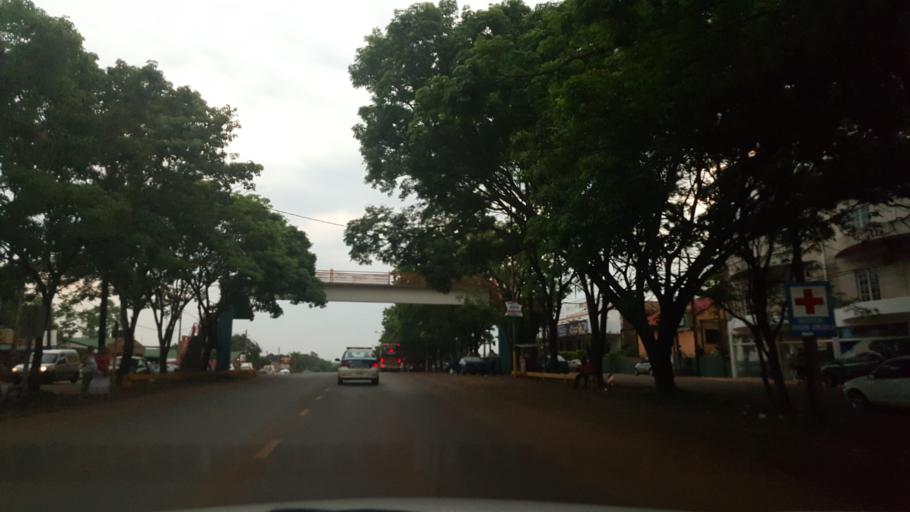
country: AR
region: Misiones
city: Jardin America
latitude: -27.0397
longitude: -55.2305
